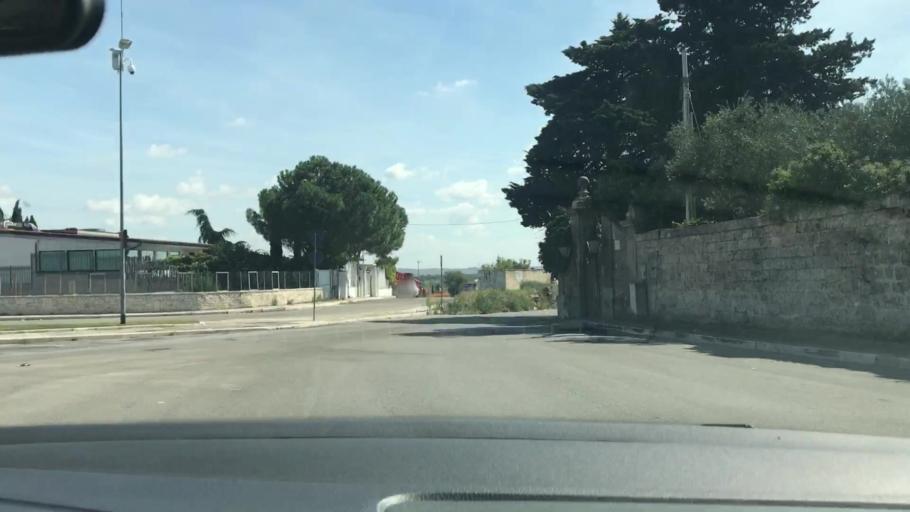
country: IT
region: Apulia
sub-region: Provincia di Bari
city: Altamura
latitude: 40.8251
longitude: 16.5668
